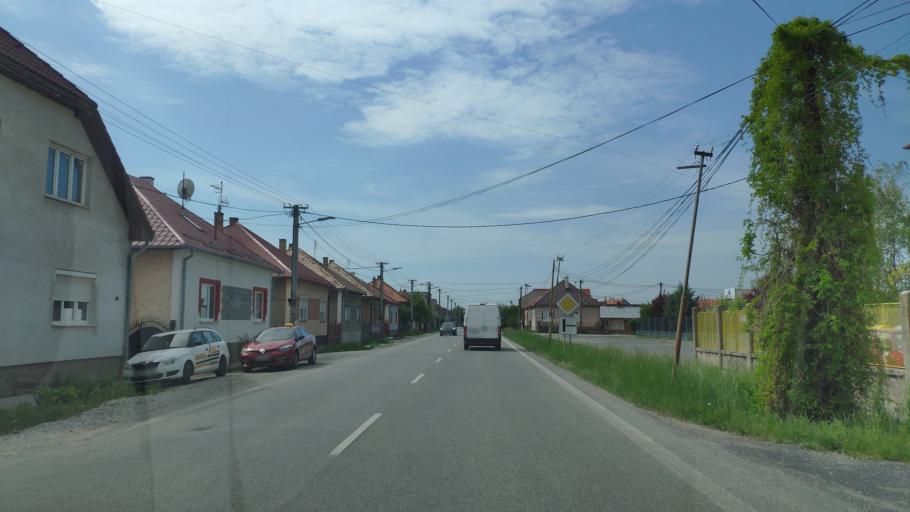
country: HU
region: Borsod-Abauj-Zemplen
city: Putnok
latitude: 48.4279
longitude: 20.3314
